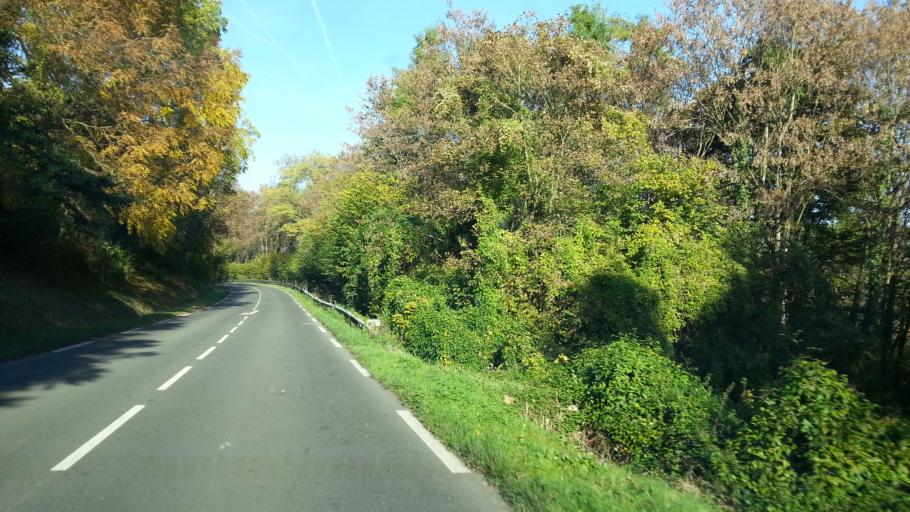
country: FR
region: Picardie
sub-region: Departement de l'Oise
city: Cires-les-Mello
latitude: 49.2828
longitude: 2.3608
